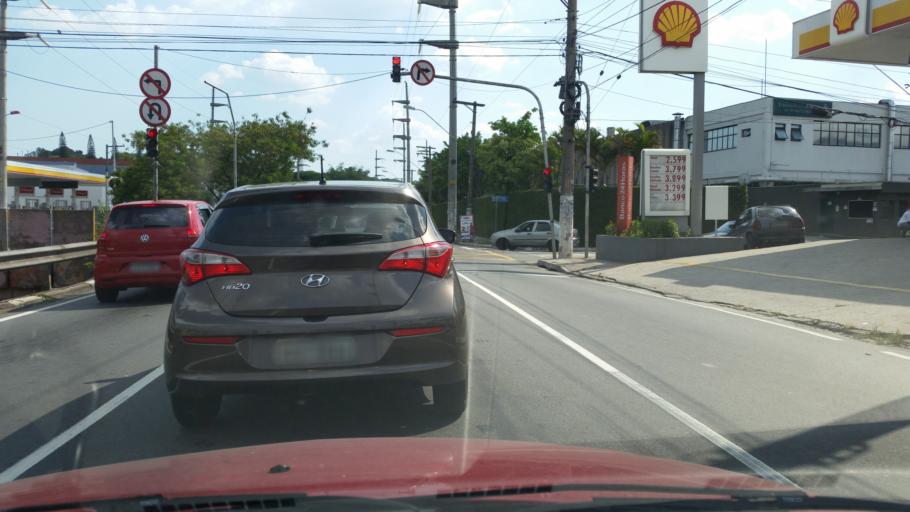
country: BR
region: Sao Paulo
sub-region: Sao Bernardo Do Campo
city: Sao Bernardo do Campo
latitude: -23.6744
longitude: -46.5868
